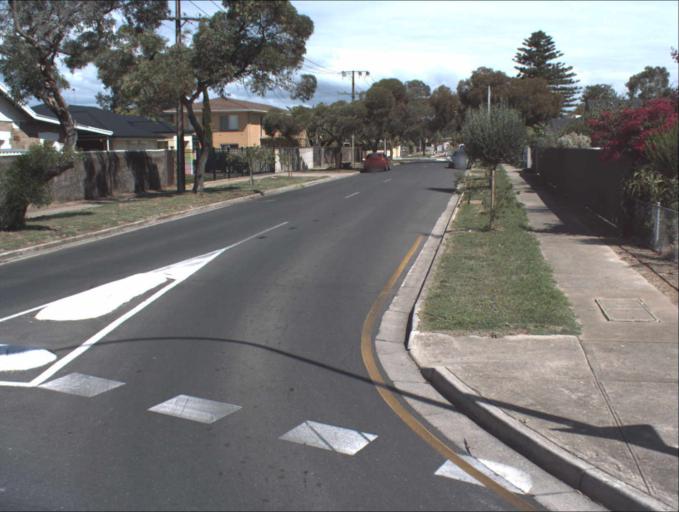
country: AU
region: South Australia
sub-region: Port Adelaide Enfield
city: Blair Athol
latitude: -34.8635
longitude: 138.5853
